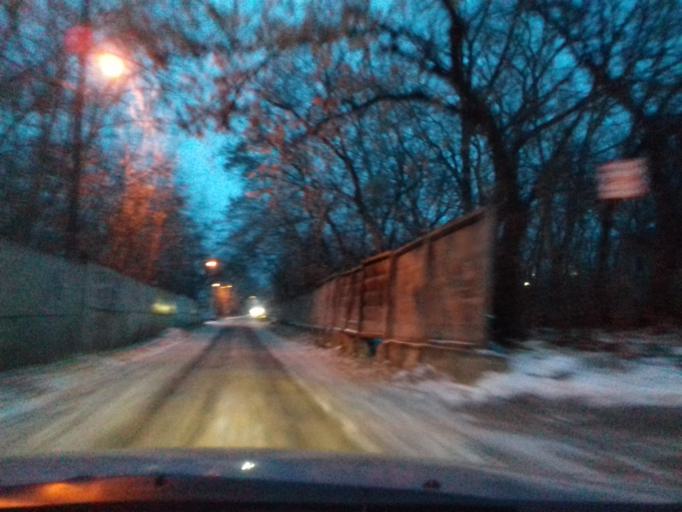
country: RU
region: Sverdlovsk
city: Istok
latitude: 56.7469
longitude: 60.6922
